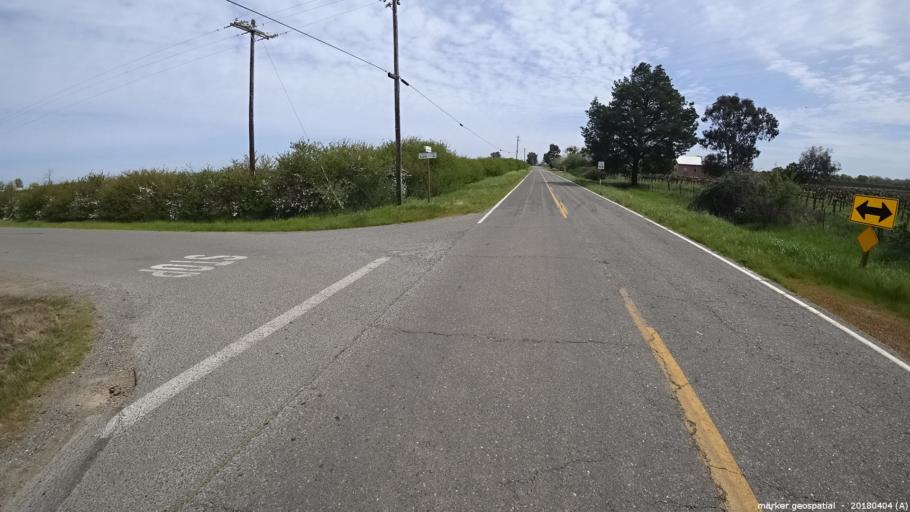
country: US
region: California
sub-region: Sacramento County
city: Herald
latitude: 38.2634
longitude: -121.1899
